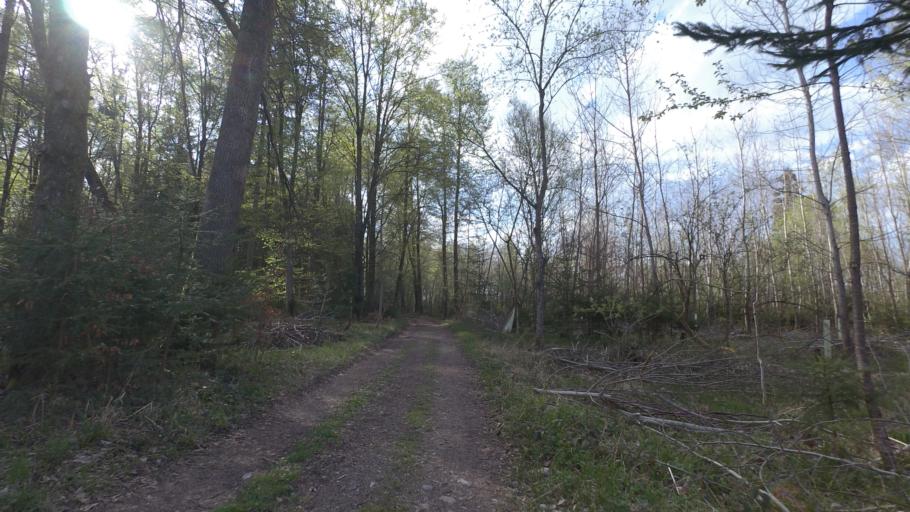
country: DE
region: Bavaria
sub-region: Upper Bavaria
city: Nussdorf
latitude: 47.8960
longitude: 12.5763
